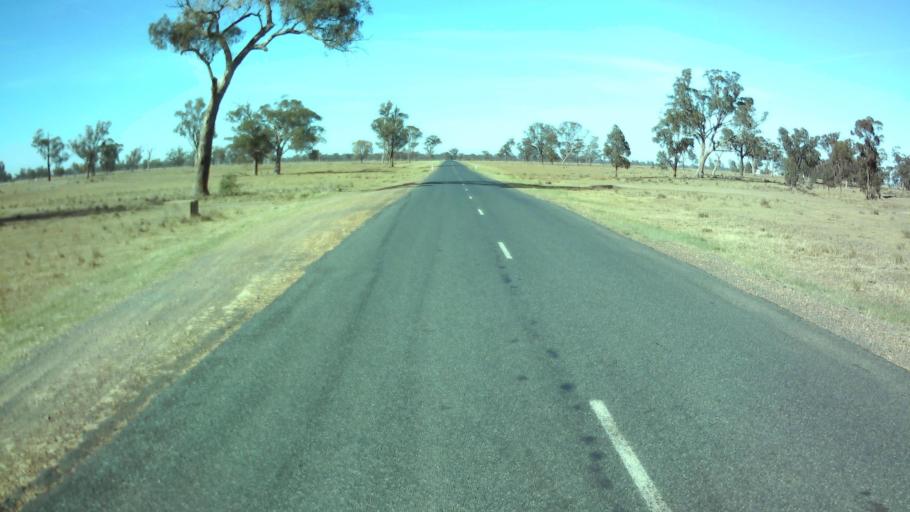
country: AU
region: New South Wales
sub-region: Weddin
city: Grenfell
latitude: -34.0443
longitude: 147.9264
